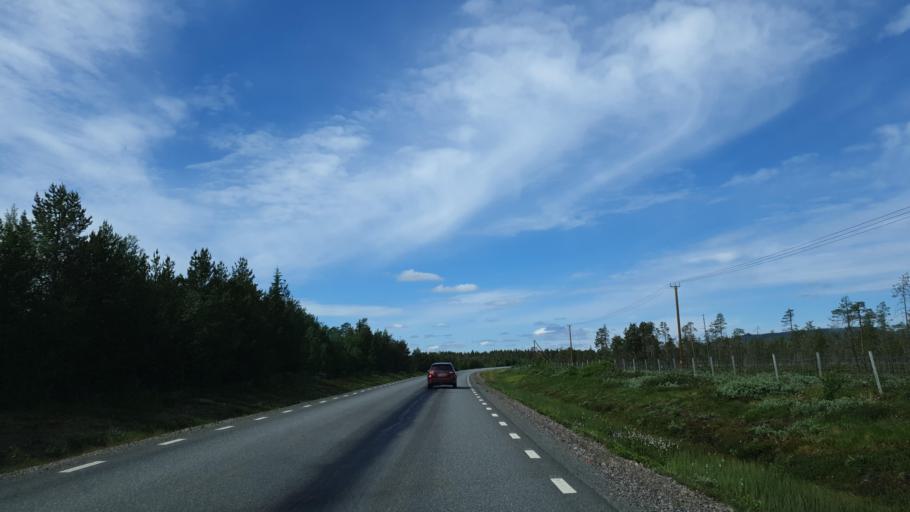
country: SE
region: Norrbotten
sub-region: Arvidsjaurs Kommun
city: Arvidsjaur
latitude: 65.5997
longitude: 18.8486
